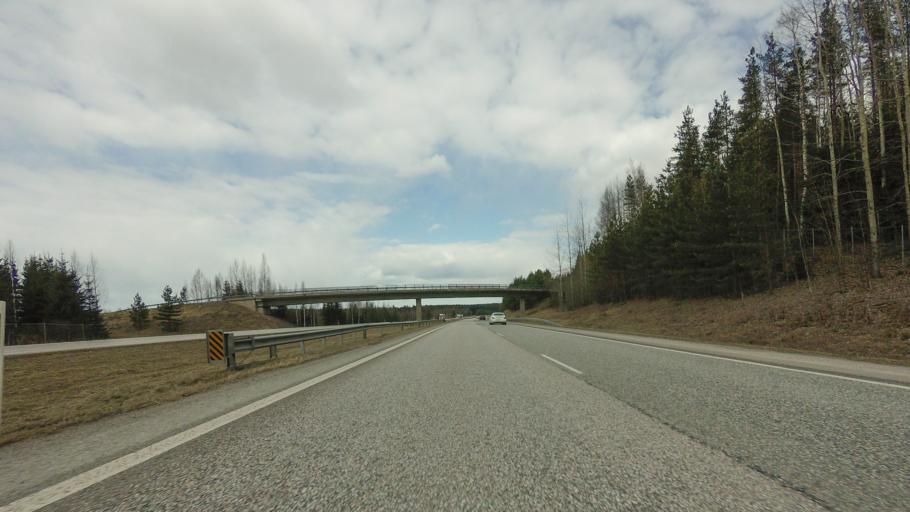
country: FI
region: Uusimaa
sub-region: Helsinki
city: Nurmijaervi
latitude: 60.4199
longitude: 24.8252
